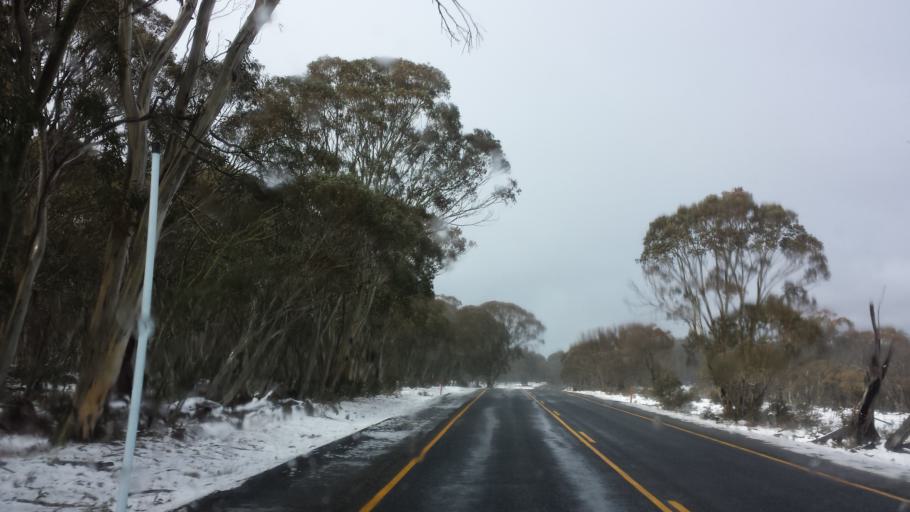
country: AU
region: Victoria
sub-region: Alpine
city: Mount Beauty
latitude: -37.0337
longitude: 147.3013
